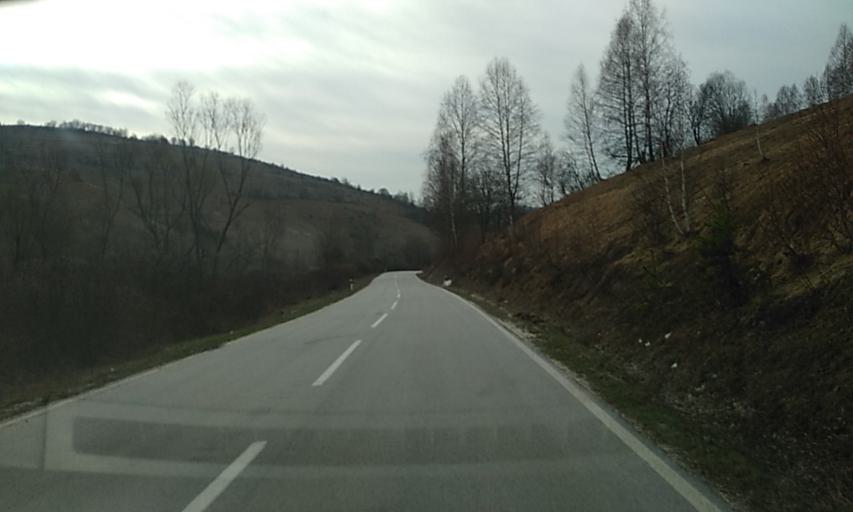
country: RS
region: Central Serbia
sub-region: Pcinjski Okrug
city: Bosilegrad
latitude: 42.6409
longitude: 22.3758
